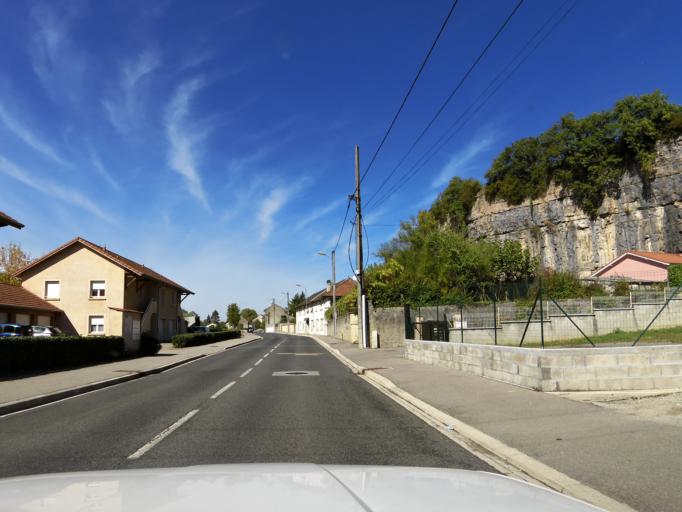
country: FR
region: Rhone-Alpes
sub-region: Departement de l'Ain
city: Sault-Brenaz
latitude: 45.8588
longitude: 5.4036
